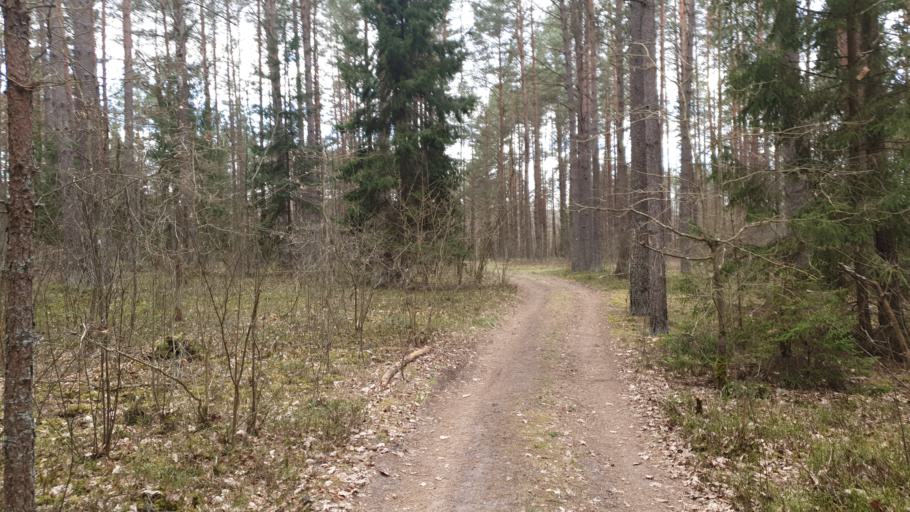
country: LT
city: Grigiskes
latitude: 54.7255
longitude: 25.0306
